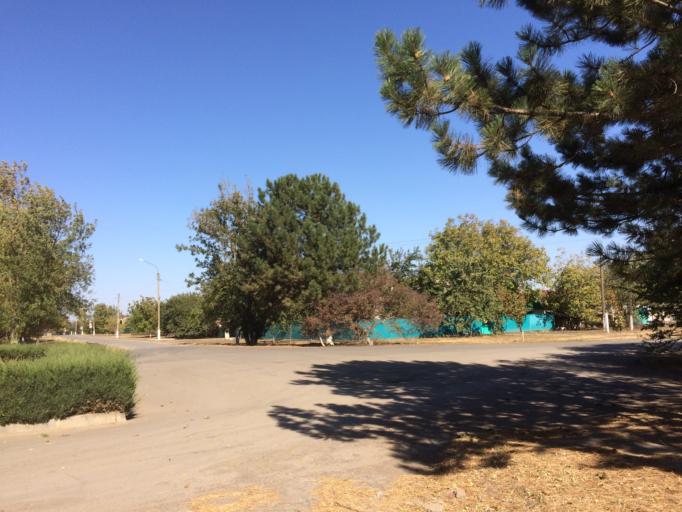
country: RU
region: Rostov
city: Tselina
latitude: 46.5158
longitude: 41.1837
